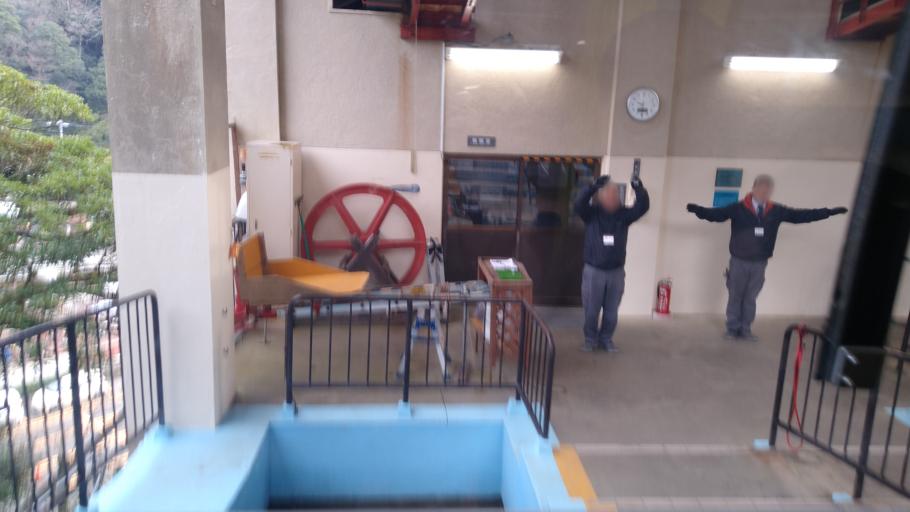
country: JP
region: Hyogo
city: Toyooka
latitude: 35.6251
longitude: 134.8036
